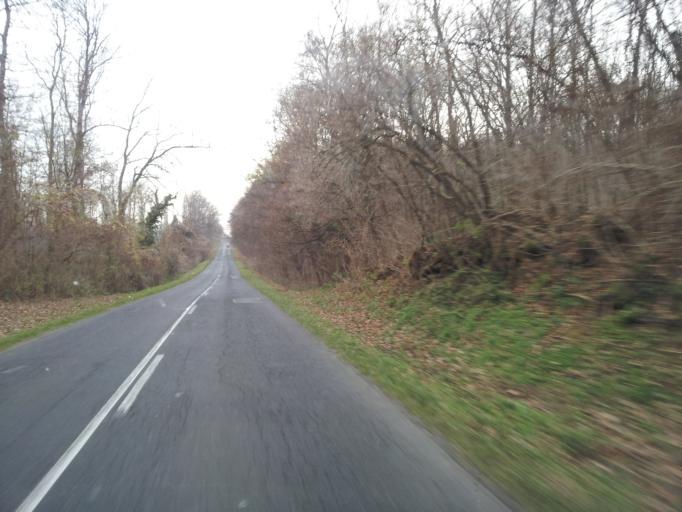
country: HU
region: Veszprem
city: Sumeg
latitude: 46.9039
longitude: 17.2383
